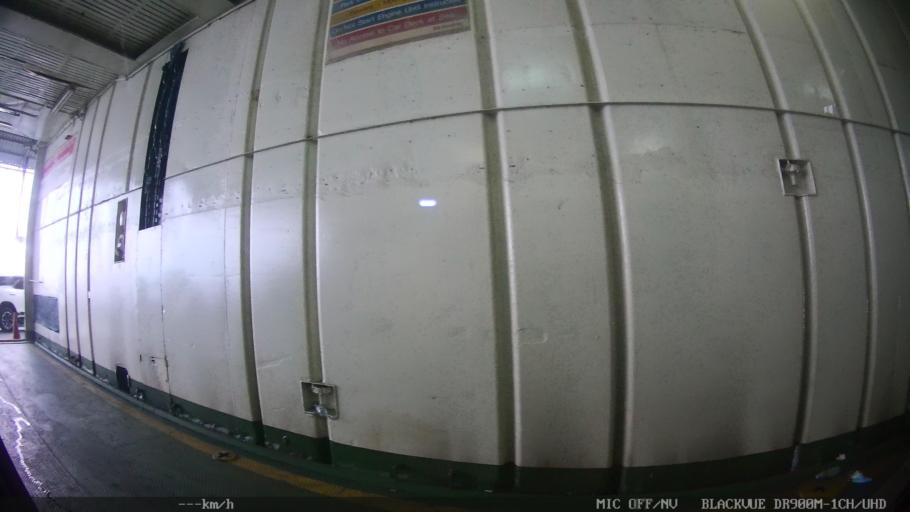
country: ID
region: Lampung
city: Penengahan
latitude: -5.8660
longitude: 105.7572
